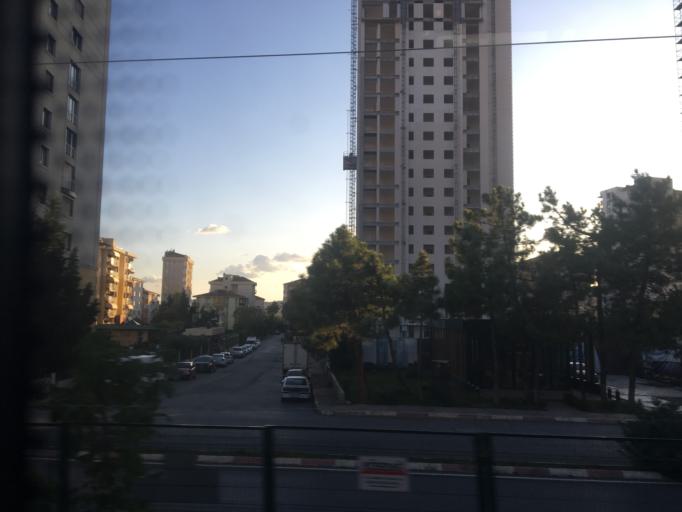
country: TR
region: Istanbul
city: Maltepe
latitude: 40.9014
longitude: 29.1662
